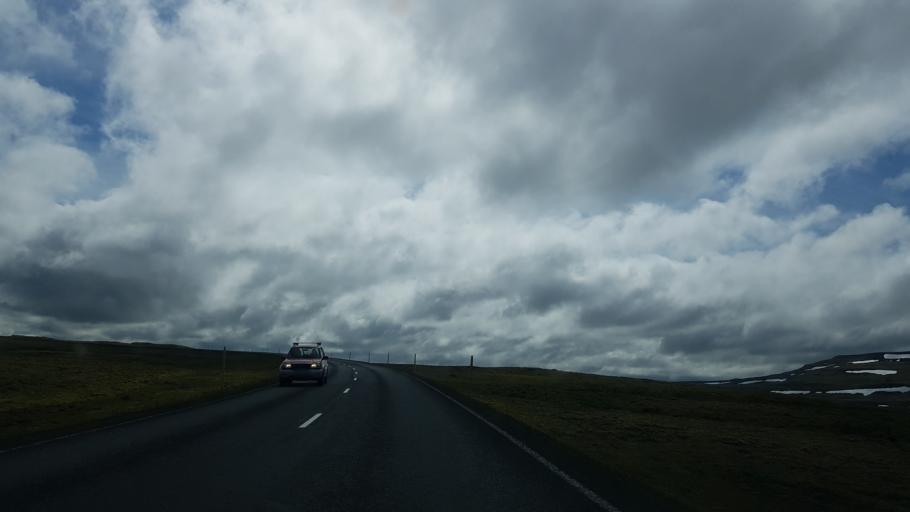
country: IS
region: West
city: Borgarnes
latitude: 65.0011
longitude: -21.0683
